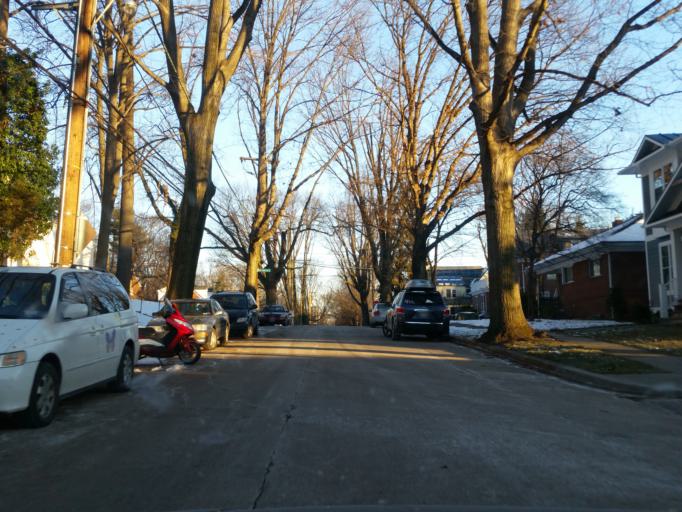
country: US
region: Maryland
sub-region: Montgomery County
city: Chevy Chase
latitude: 38.9689
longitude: -77.0638
